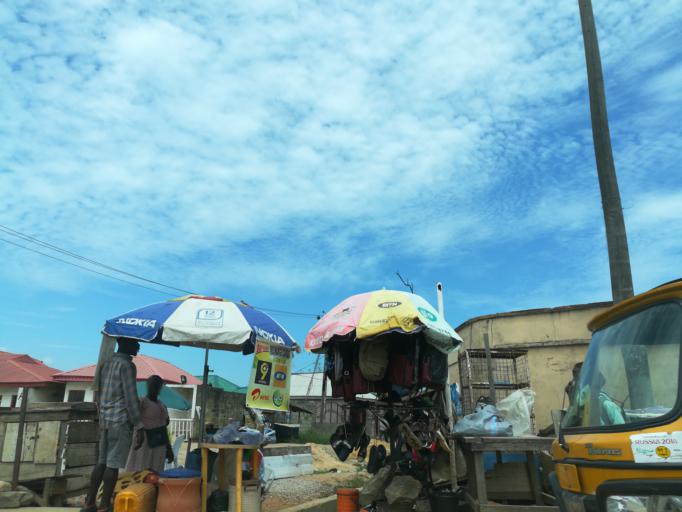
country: NG
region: Lagos
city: Ebute Ikorodu
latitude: 6.5586
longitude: 3.4758
